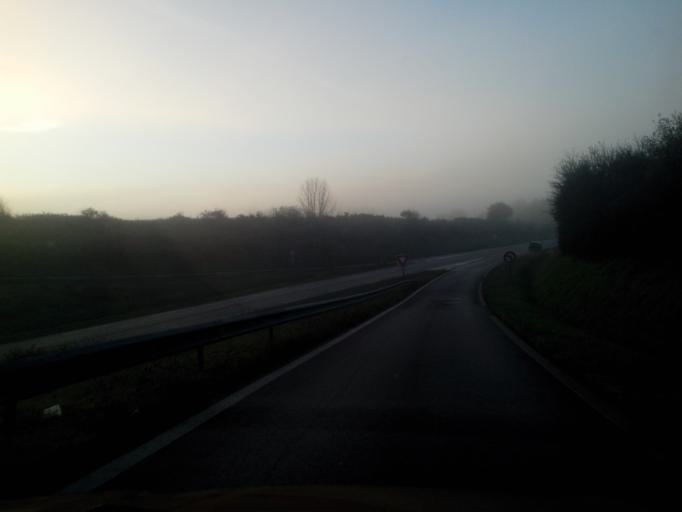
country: FR
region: Brittany
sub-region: Departement du Morbihan
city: Mauron
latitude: 48.0817
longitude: -2.2698
